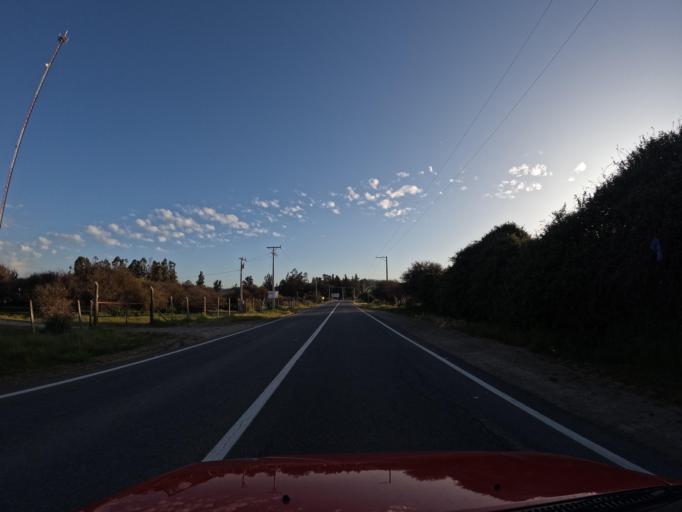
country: CL
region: O'Higgins
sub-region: Provincia de Colchagua
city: Santa Cruz
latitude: -34.3296
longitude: -71.7456
